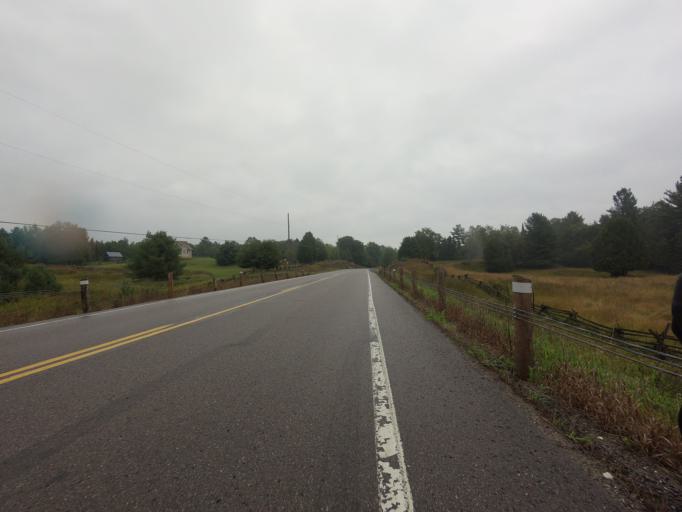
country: CA
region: Ontario
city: Carleton Place
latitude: 45.1081
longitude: -76.3790
